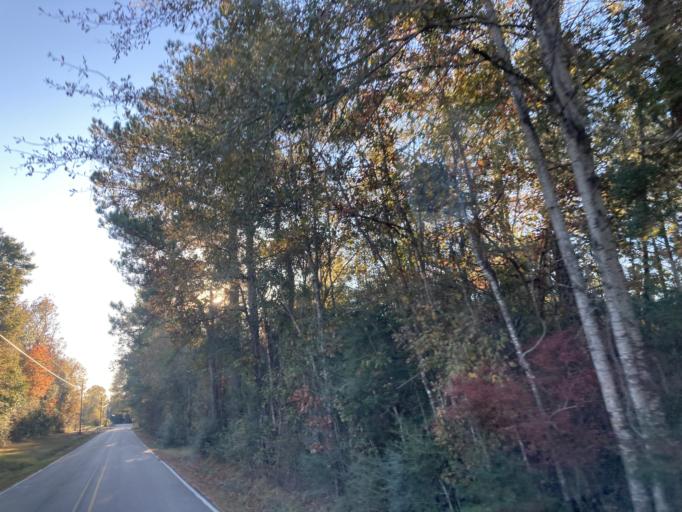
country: US
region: Mississippi
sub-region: Marion County
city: Columbia
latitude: 31.2395
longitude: -89.6367
